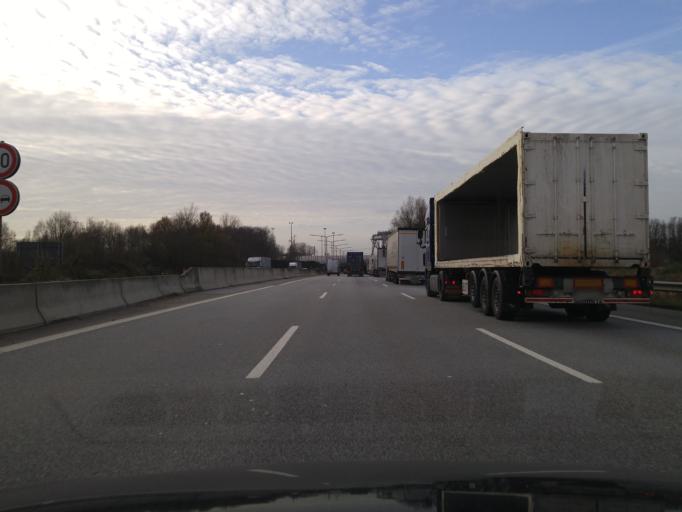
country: DE
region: Hamburg
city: Wandsbek
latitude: 53.5139
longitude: 10.1095
